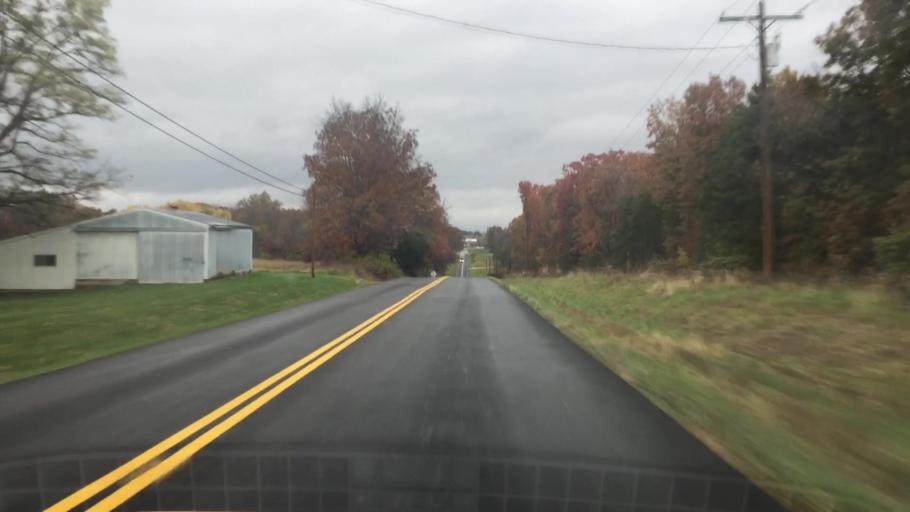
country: US
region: Missouri
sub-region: Boone County
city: Columbia
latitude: 38.9625
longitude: -92.4958
